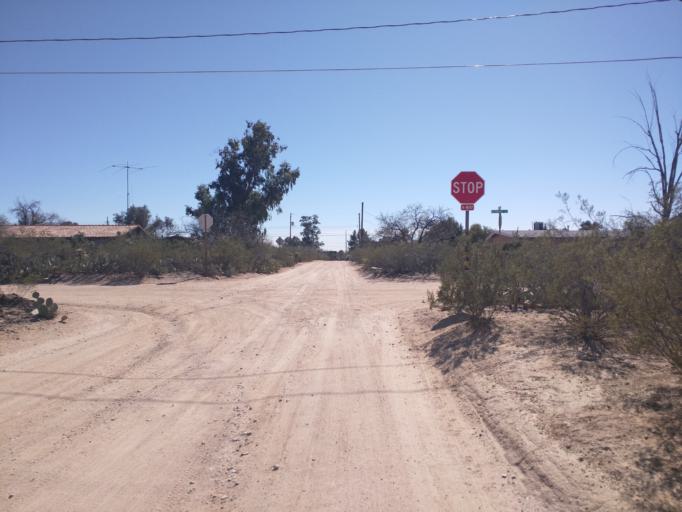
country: US
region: Arizona
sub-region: Pima County
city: Catalina Foothills
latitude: 32.2688
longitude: -110.9503
